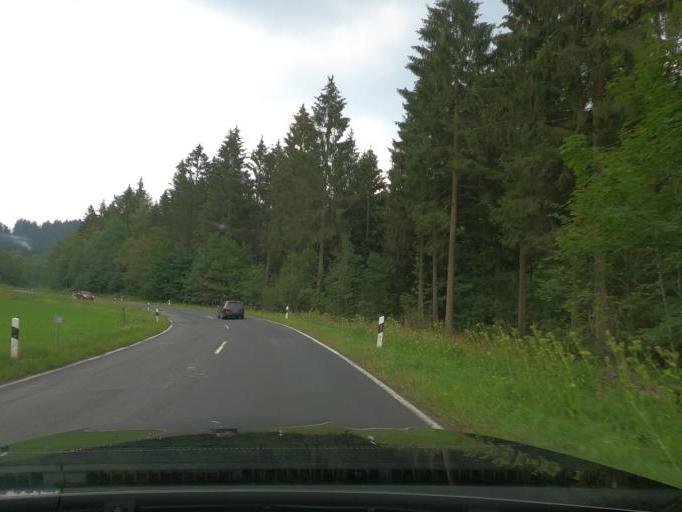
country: DE
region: Lower Saxony
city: Wildemann
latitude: 51.8353
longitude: 10.2667
